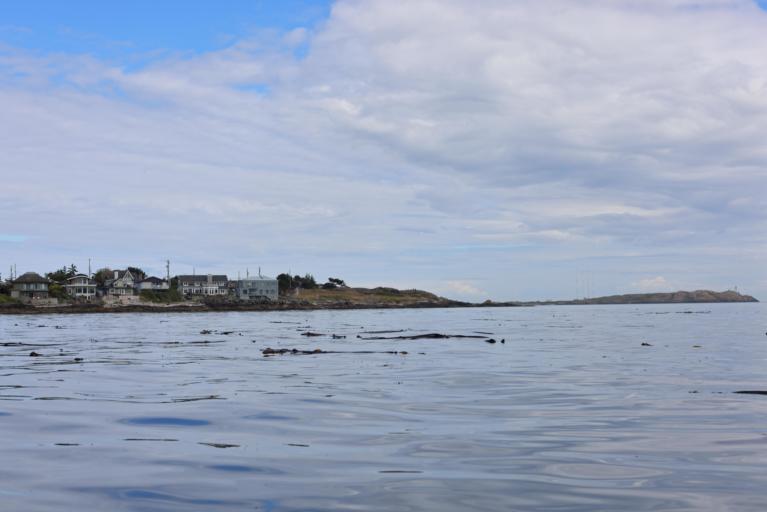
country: CA
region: British Columbia
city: Victoria
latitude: 48.4079
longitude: -123.3298
